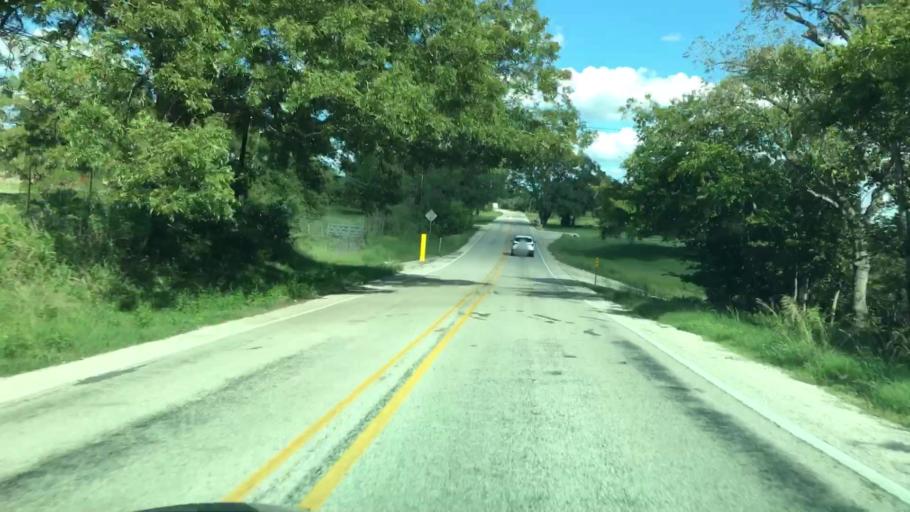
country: US
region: Texas
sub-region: Blanco County
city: Blanco
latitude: 30.0916
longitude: -98.3767
